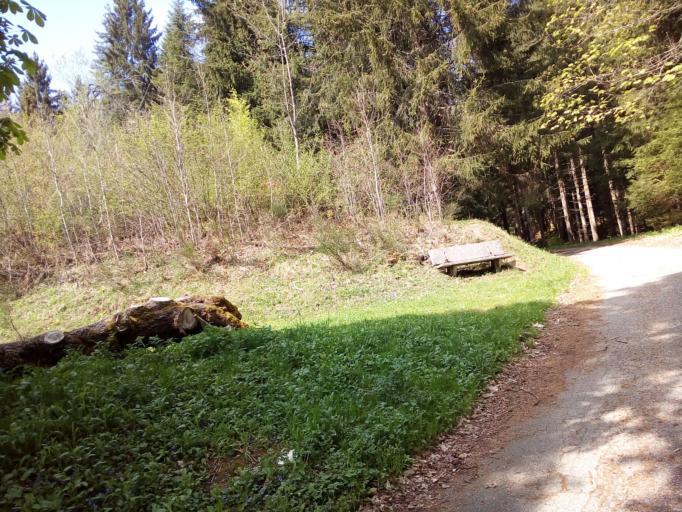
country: FR
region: Rhone-Alpes
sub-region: Departement de l'Isere
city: Revel
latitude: 45.1423
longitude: 5.8677
